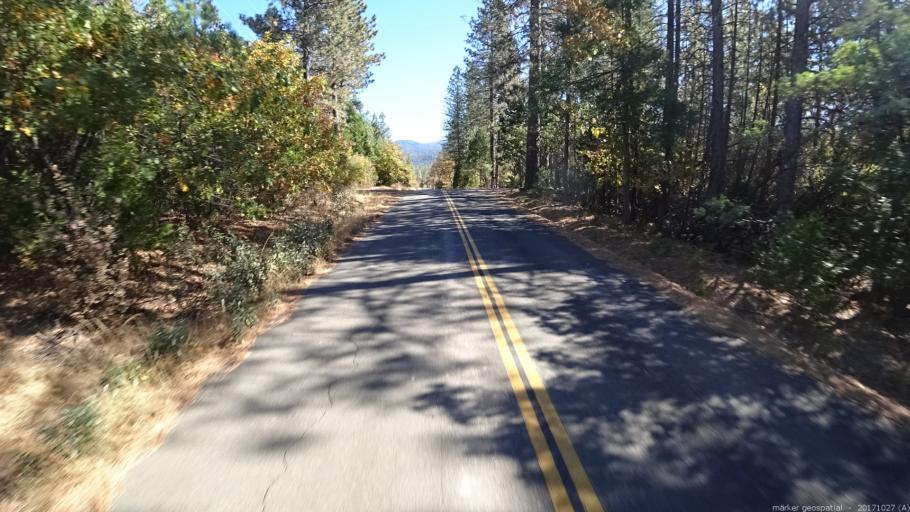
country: US
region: California
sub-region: Shasta County
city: Shingletown
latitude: 40.7521
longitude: -121.9570
